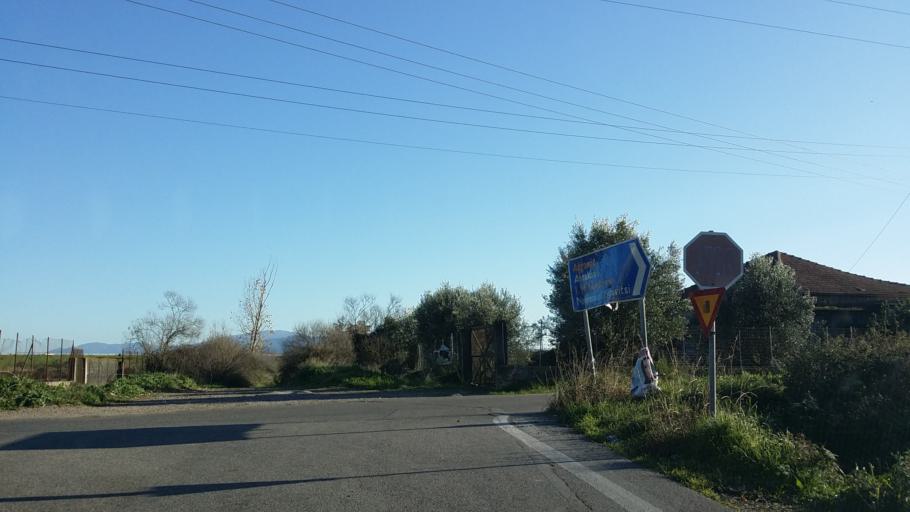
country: GR
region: West Greece
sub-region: Nomos Aitolias kai Akarnanias
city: Angelokastro
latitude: 38.6178
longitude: 21.2272
